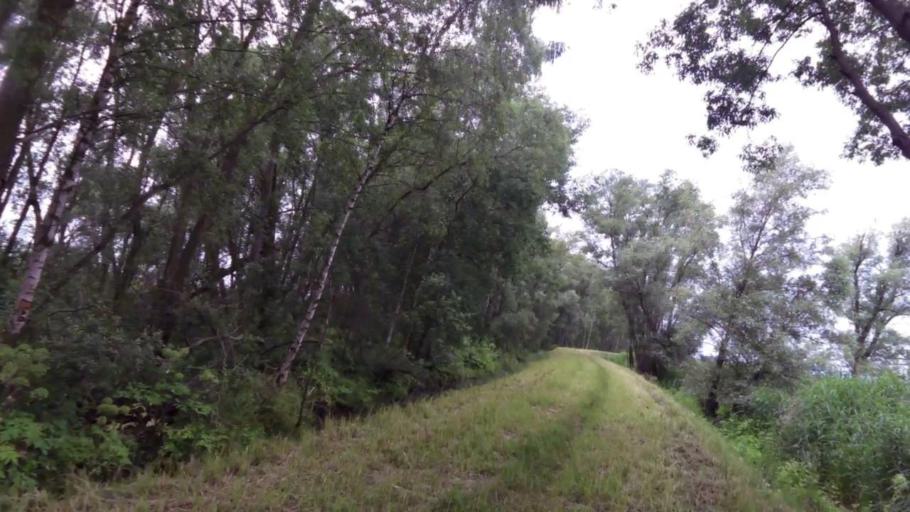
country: PL
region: West Pomeranian Voivodeship
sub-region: Szczecin
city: Szczecin
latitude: 53.4323
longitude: 14.6630
